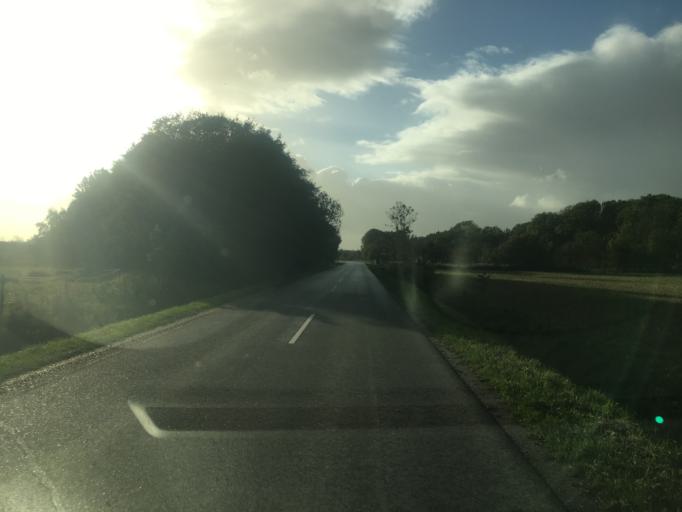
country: DE
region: Schleswig-Holstein
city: Aventoft
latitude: 54.9221
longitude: 8.7906
